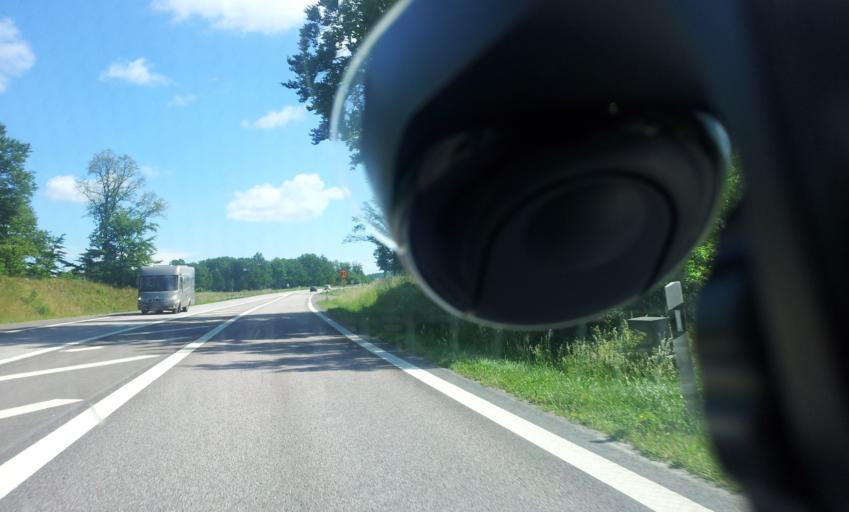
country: SE
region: Kalmar
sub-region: Monsteras Kommun
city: Moensteras
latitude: 57.0599
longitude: 16.4444
